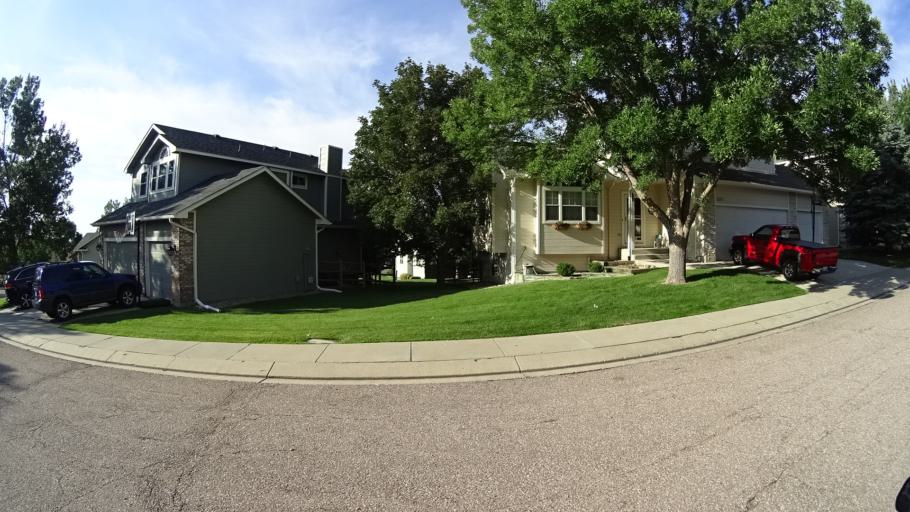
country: US
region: Colorado
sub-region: El Paso County
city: Air Force Academy
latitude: 38.9251
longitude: -104.8486
